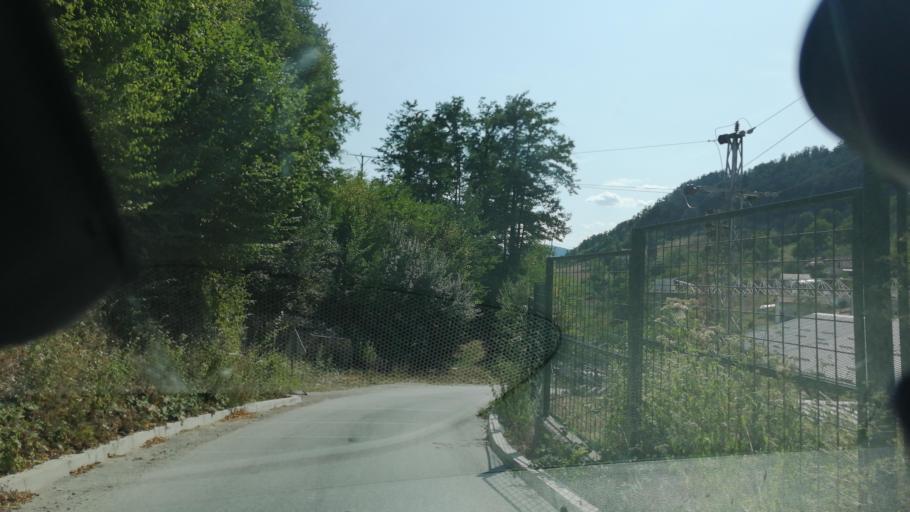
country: RS
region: Central Serbia
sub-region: Moravicki Okrug
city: Ivanjica
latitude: 43.6255
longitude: 20.2412
